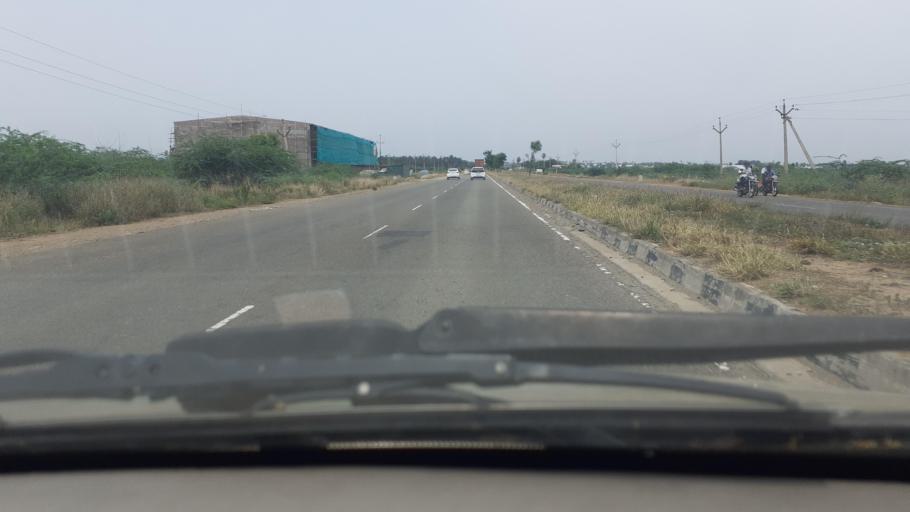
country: IN
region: Tamil Nadu
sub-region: Thoothukkudi
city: Eral
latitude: 8.7346
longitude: 77.9779
